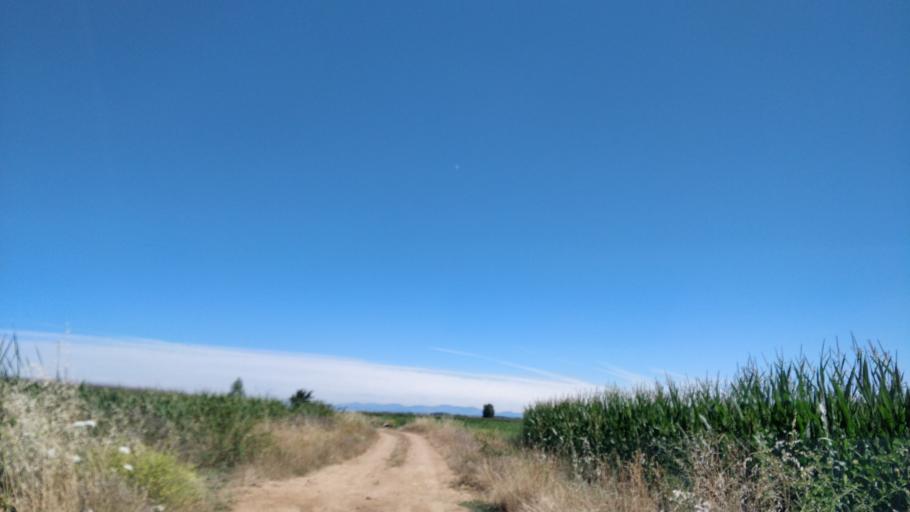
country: ES
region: Castille and Leon
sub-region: Provincia de Leon
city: Bustillo del Paramo
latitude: 42.4443
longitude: -5.8151
